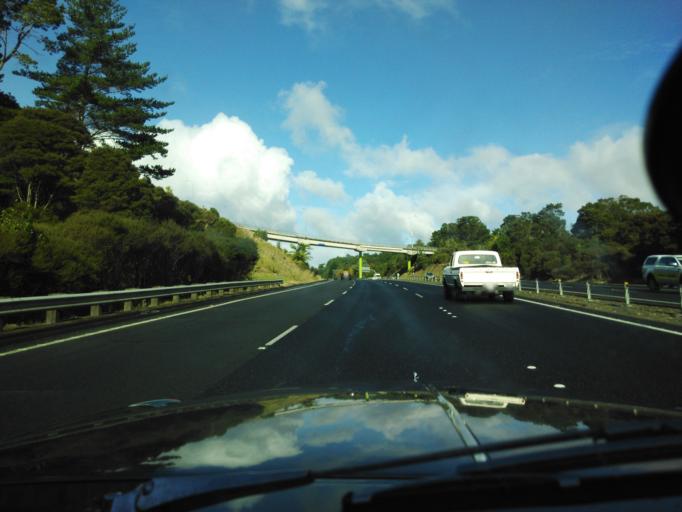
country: NZ
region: Auckland
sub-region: Auckland
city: Rothesay Bay
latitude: -36.7083
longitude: 174.7064
